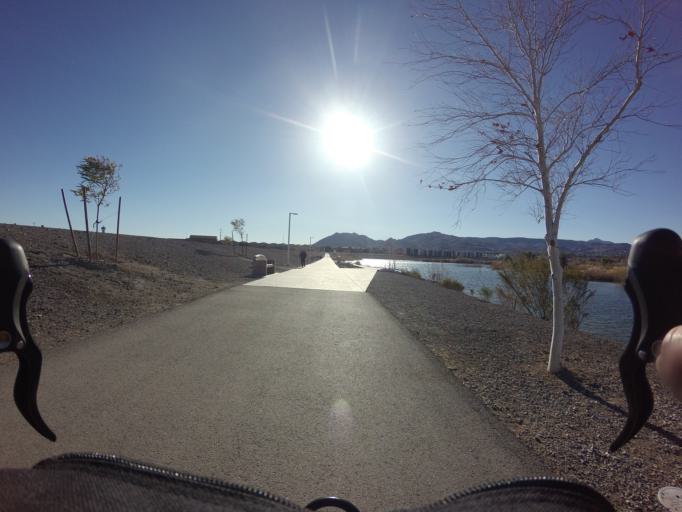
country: US
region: Nevada
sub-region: Clark County
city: Whitney
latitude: 36.0399
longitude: -115.0534
